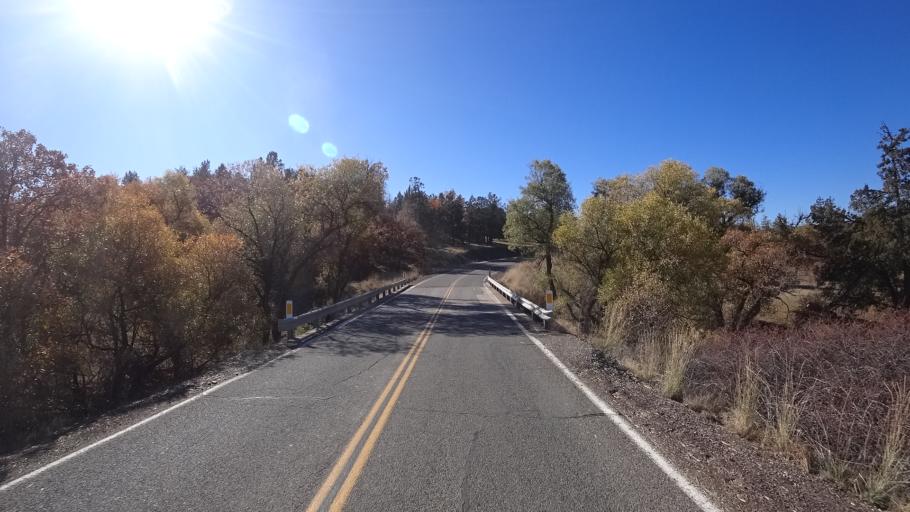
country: US
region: California
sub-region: Siskiyou County
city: Montague
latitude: 41.8075
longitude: -122.3834
